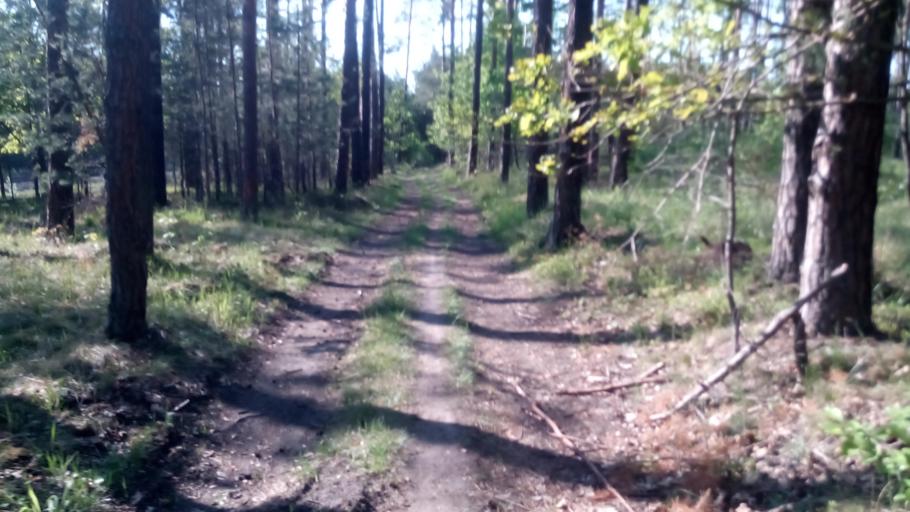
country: PL
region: Opole Voivodeship
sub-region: Powiat opolski
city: Tarnow Opolski
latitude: 50.5868
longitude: 18.0504
